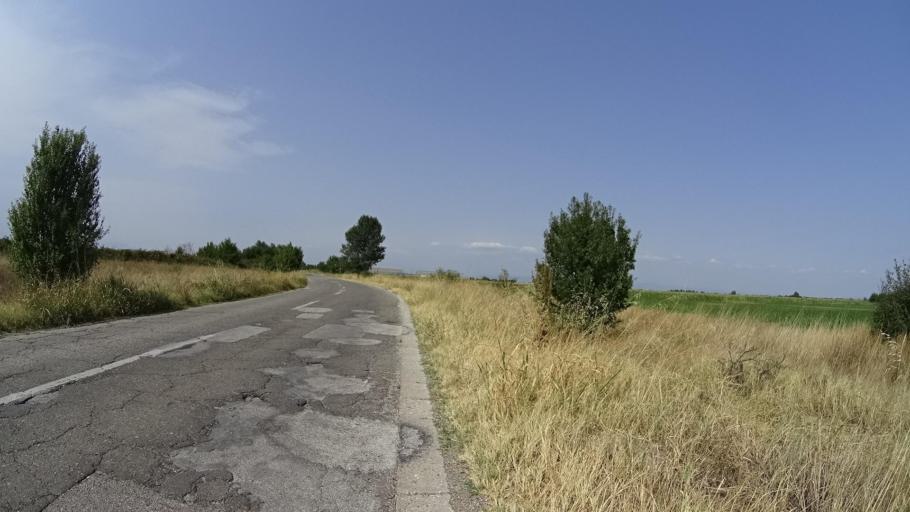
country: BG
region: Plovdiv
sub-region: Obshtina Plovdiv
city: Plovdiv
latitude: 42.2265
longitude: 24.7861
